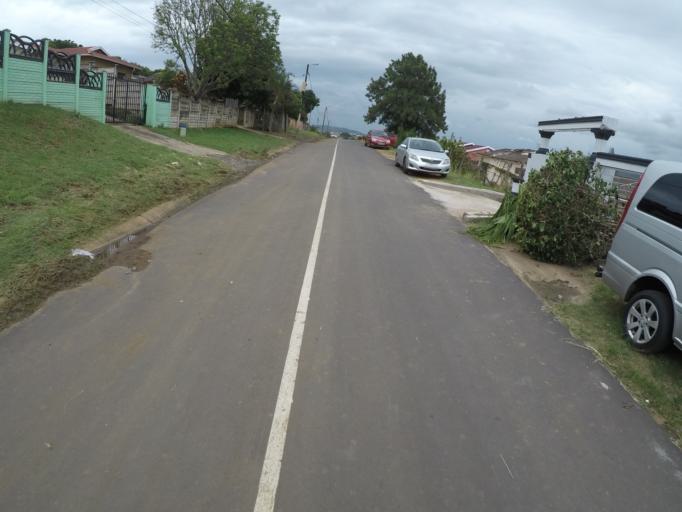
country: ZA
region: KwaZulu-Natal
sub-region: uThungulu District Municipality
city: Empangeni
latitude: -28.7843
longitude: 31.8566
